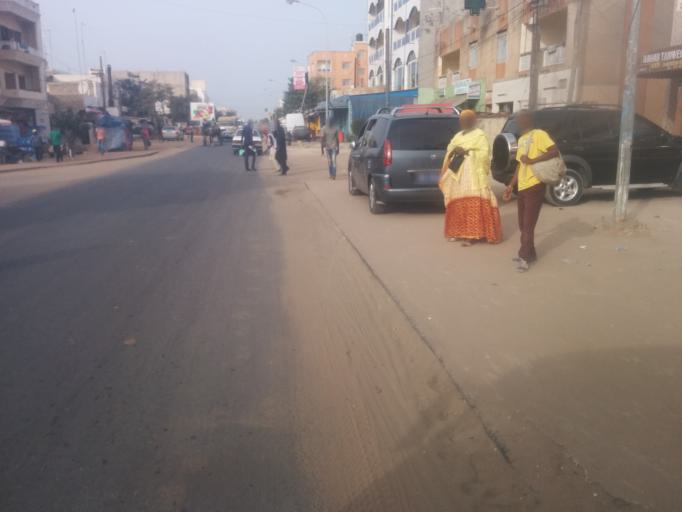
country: SN
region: Dakar
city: Pikine
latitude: 14.7607
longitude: -17.4394
